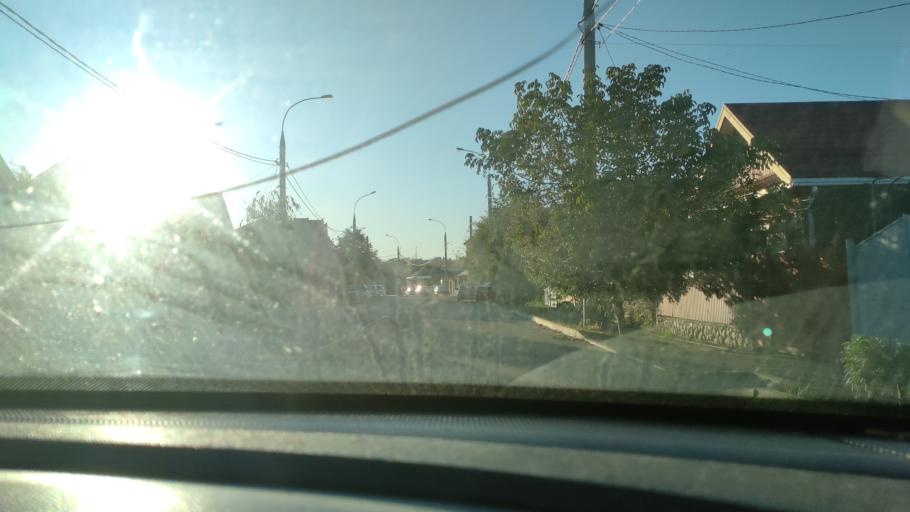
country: RU
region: Krasnodarskiy
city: Krasnodar
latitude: 45.0417
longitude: 38.9321
